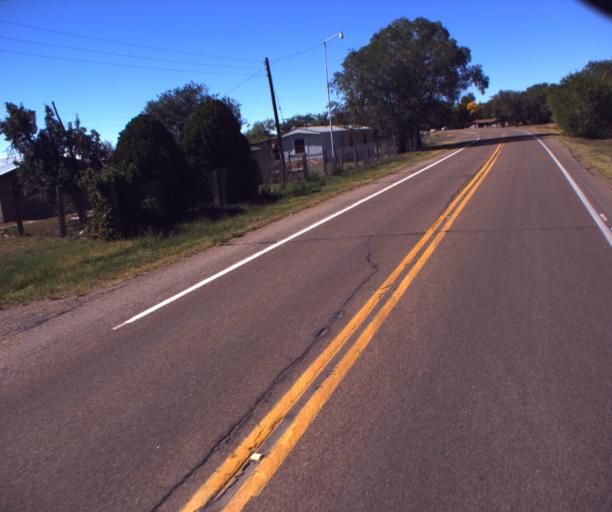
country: US
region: Arizona
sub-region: Apache County
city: Saint Johns
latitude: 34.4992
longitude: -109.3660
